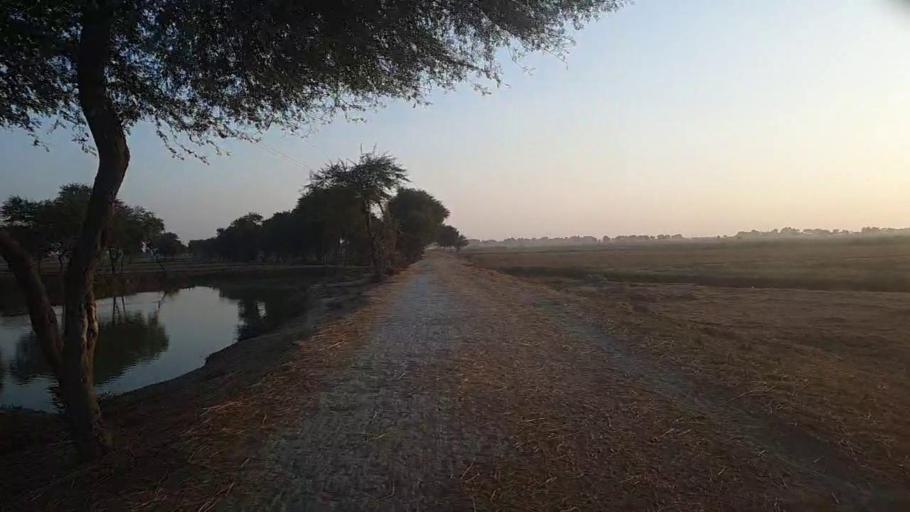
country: PK
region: Sindh
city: Khairpur Nathan Shah
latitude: 27.1685
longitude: 67.7325
